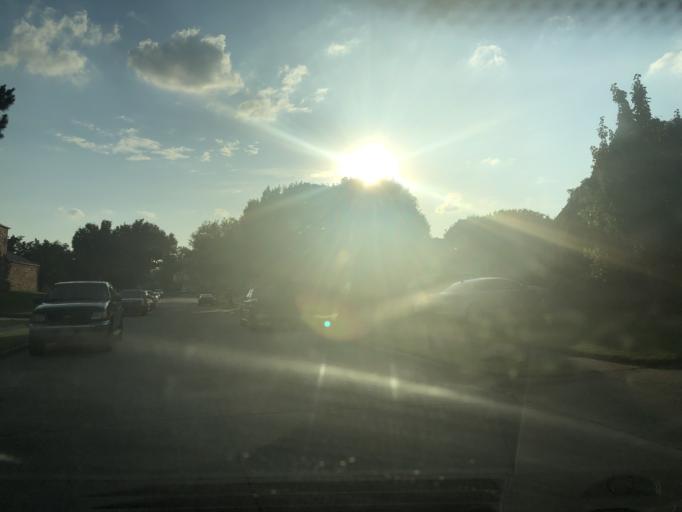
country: US
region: Texas
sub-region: Dallas County
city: Irving
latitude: 32.7852
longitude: -96.9606
